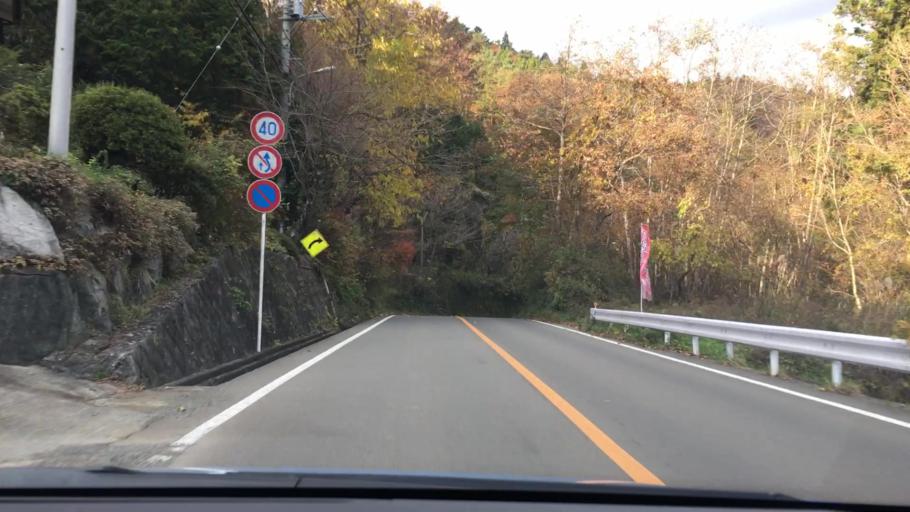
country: JP
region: Yamanashi
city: Otsuki
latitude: 35.4770
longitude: 138.9517
